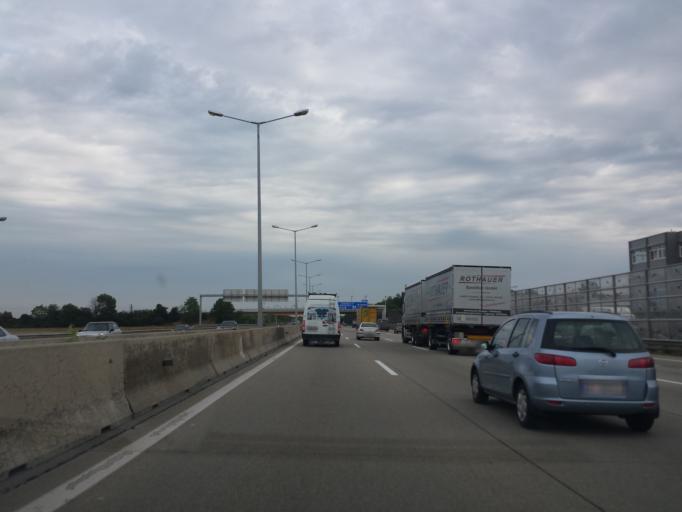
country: AT
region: Lower Austria
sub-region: Politischer Bezirk Modling
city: Wiener Neudorf
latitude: 48.0941
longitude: 16.3249
